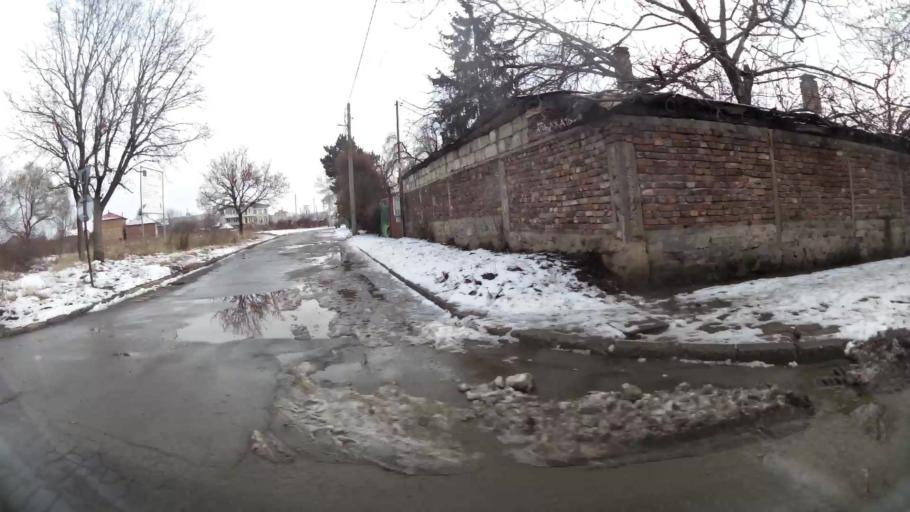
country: BG
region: Sofia-Capital
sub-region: Stolichna Obshtina
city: Sofia
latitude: 42.7155
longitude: 23.3508
